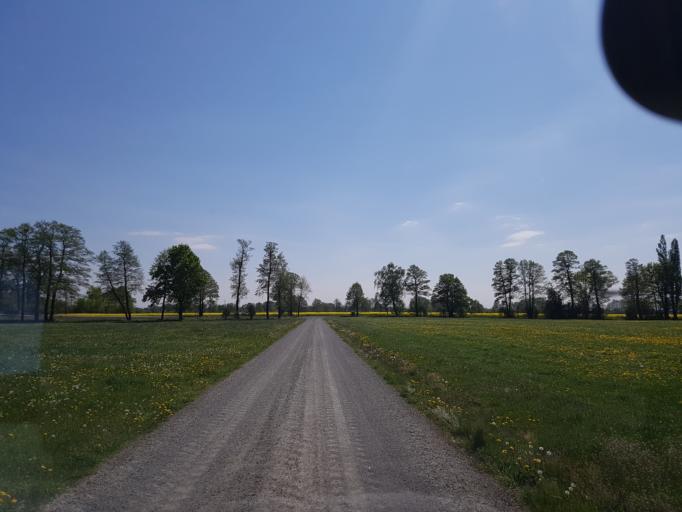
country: DE
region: Brandenburg
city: Schonewalde
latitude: 51.6691
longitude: 13.5808
